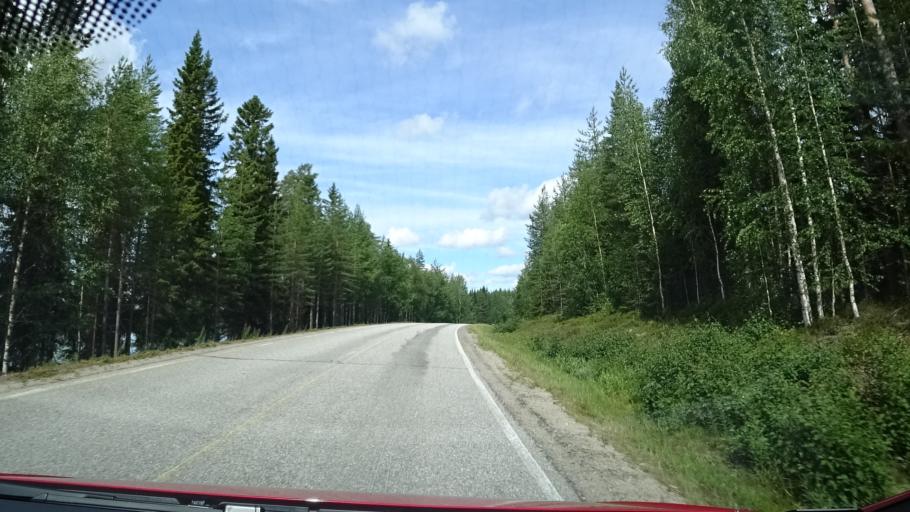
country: FI
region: Kainuu
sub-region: Kehys-Kainuu
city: Kuhmo
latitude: 64.4535
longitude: 29.7743
